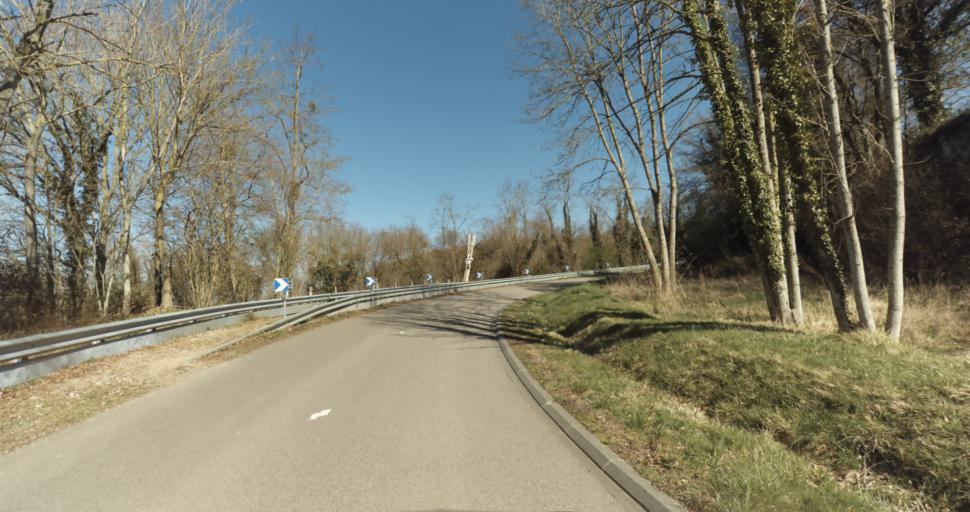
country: FR
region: Lower Normandy
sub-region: Departement du Calvados
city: Livarot
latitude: 48.9697
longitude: 0.0676
